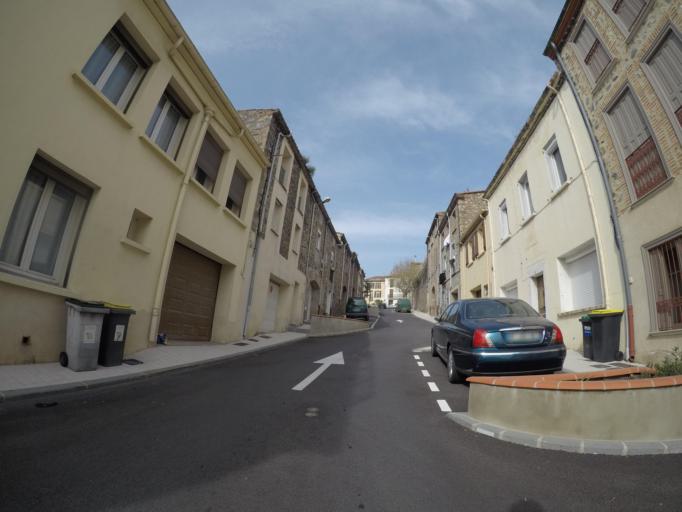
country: FR
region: Languedoc-Roussillon
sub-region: Departement des Pyrenees-Orientales
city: Baixas
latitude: 42.7789
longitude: 2.7871
